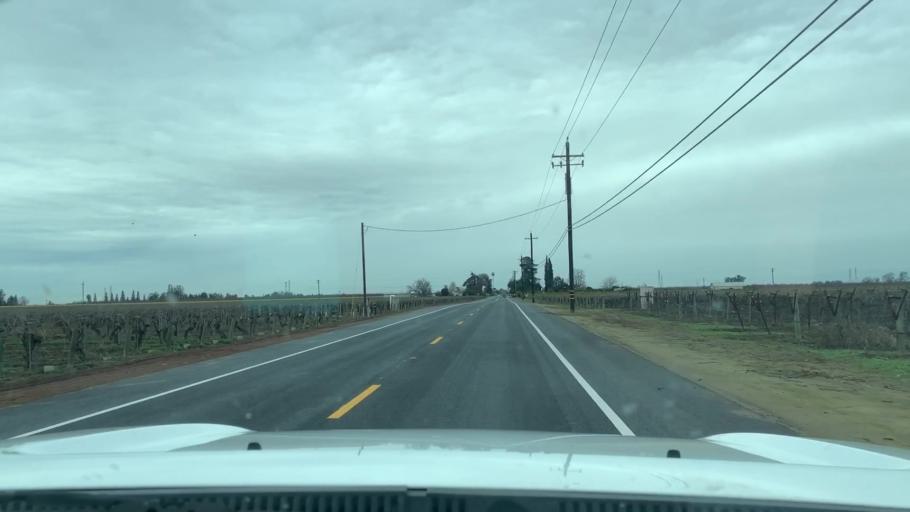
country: US
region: California
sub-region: Fresno County
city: Fowler
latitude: 36.5805
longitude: -119.6825
